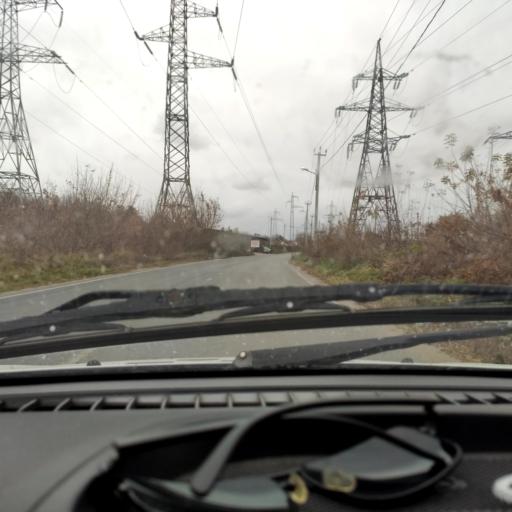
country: RU
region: Samara
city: Zhigulevsk
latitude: 53.5205
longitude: 49.4860
